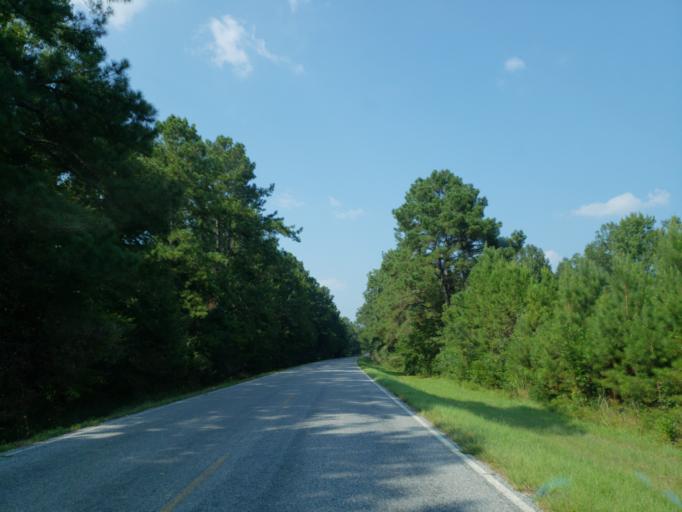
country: US
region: Mississippi
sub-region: Clarke County
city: Quitman
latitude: 31.9796
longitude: -88.9059
